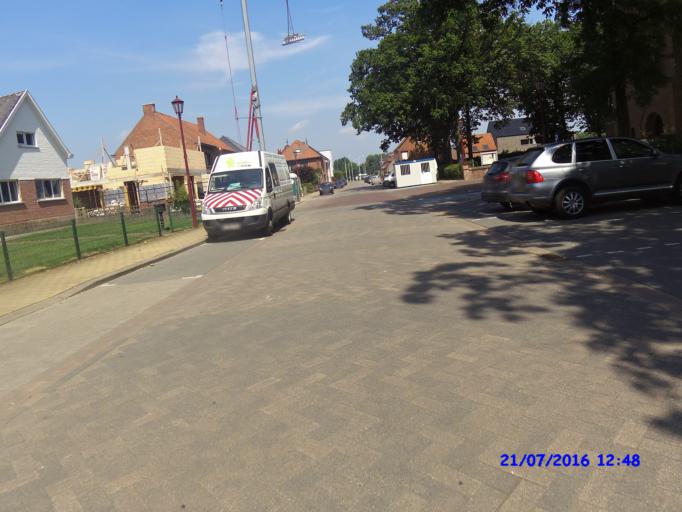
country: BE
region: Flanders
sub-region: Provincie Antwerpen
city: Kasterlee
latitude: 51.2038
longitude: 4.9792
